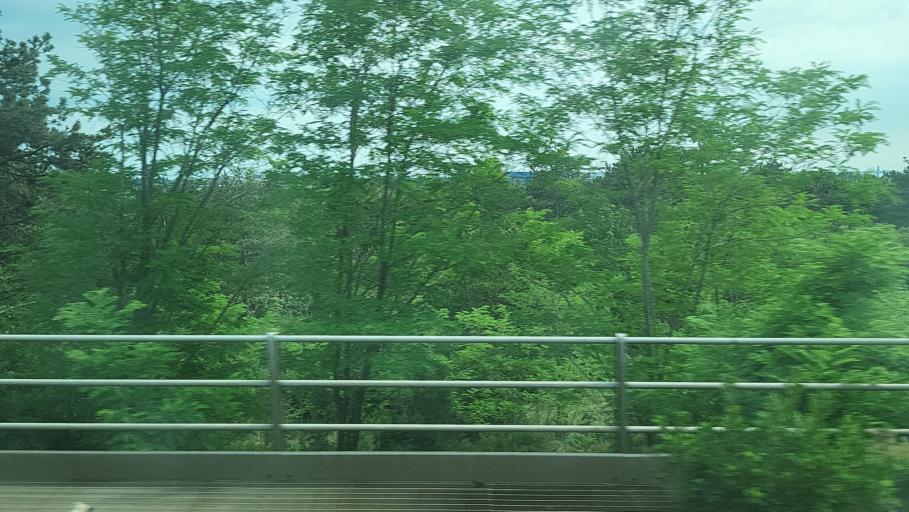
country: IT
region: Friuli Venezia Giulia
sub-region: Provincia di Gorizia
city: Monfalcone
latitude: 45.8029
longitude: 13.5711
